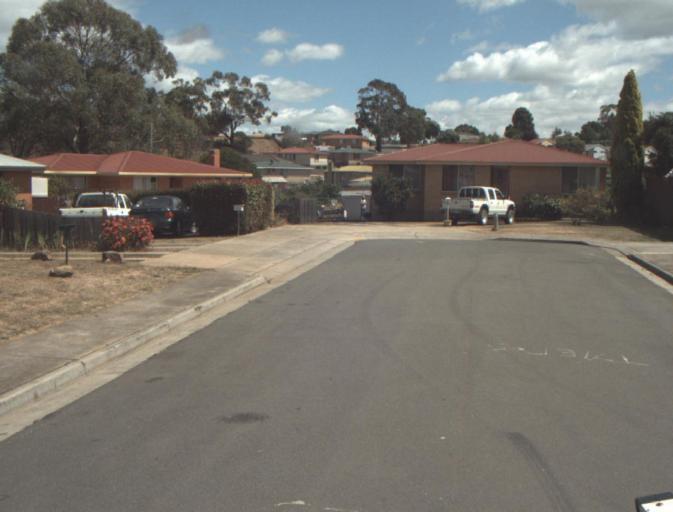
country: AU
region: Tasmania
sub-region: Launceston
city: Newstead
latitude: -41.4117
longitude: 147.1687
